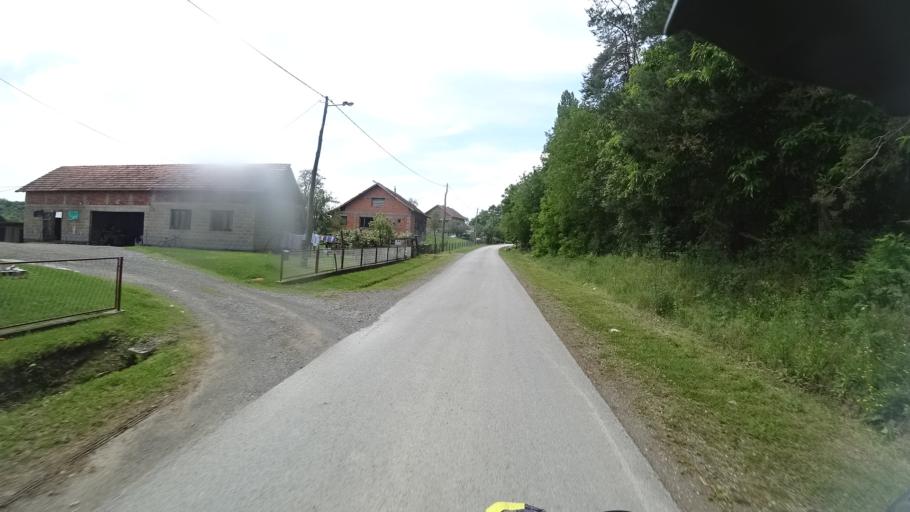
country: HR
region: Sisacko-Moslavacka
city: Gvozd
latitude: 45.3364
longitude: 15.8513
